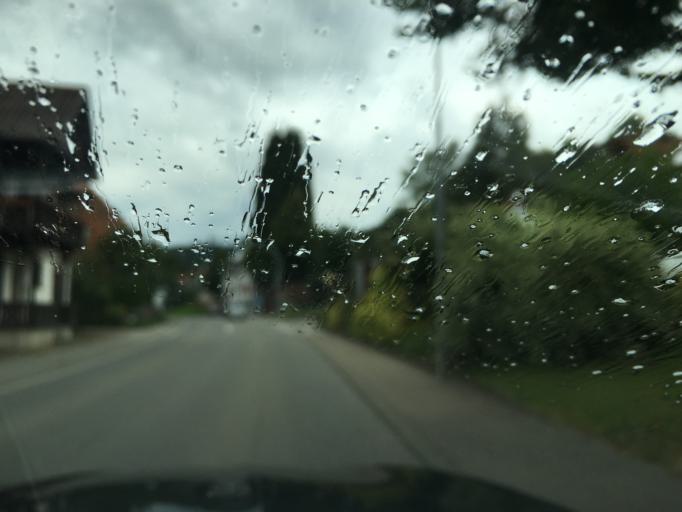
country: DE
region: Baden-Wuerttemberg
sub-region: Tuebingen Region
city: Rot
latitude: 47.8624
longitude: 9.0975
